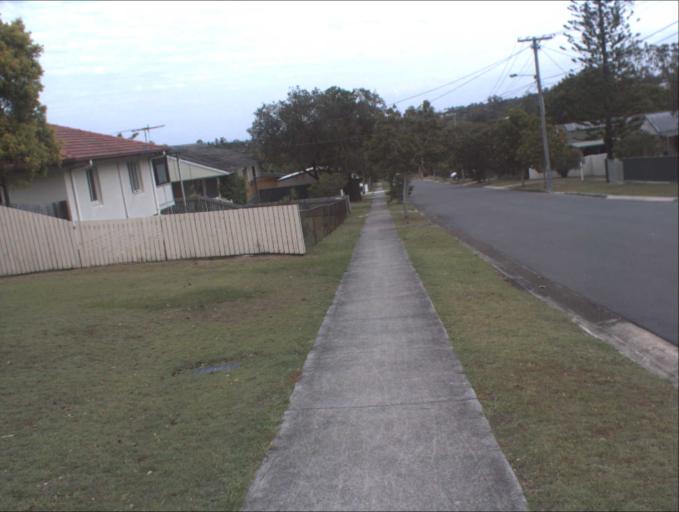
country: AU
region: Queensland
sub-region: Logan
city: Logan City
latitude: -27.6299
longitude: 153.1117
